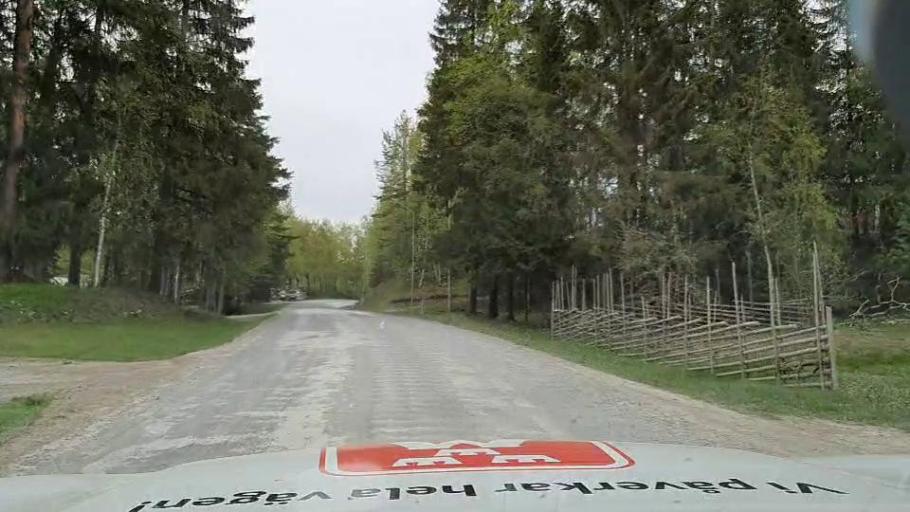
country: SE
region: Jaemtland
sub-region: OEstersunds Kommun
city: Ostersund
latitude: 62.9693
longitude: 14.6495
